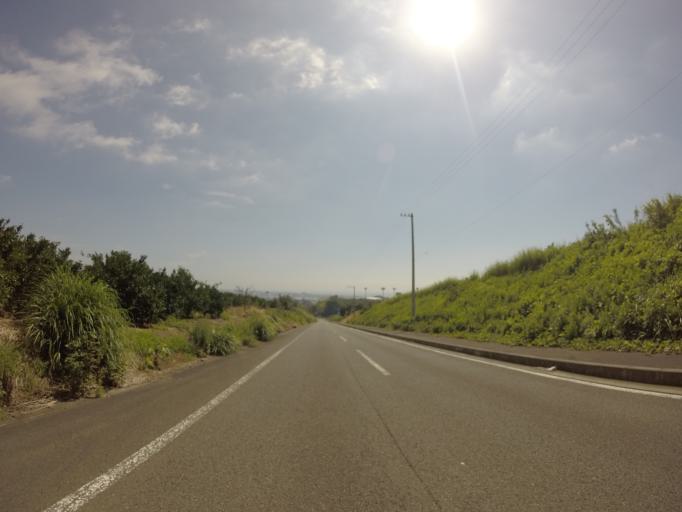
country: JP
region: Shizuoka
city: Shizuoka-shi
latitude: 34.9862
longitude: 138.4729
